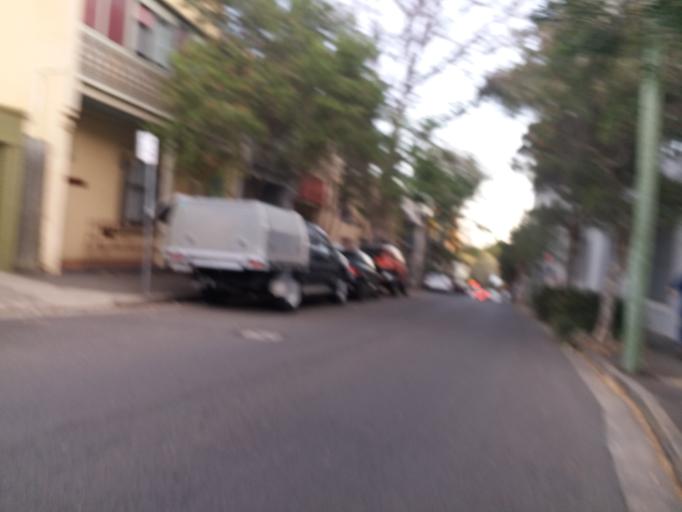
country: AU
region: New South Wales
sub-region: City of Sydney
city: Redfern
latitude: -33.8895
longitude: 151.2116
